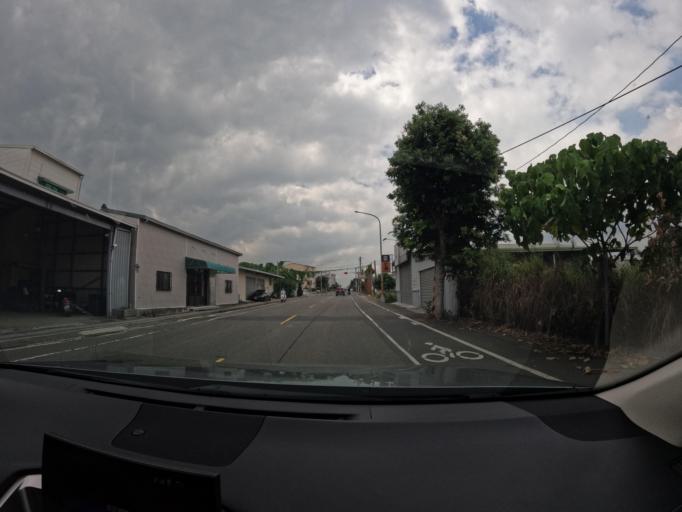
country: TW
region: Taiwan
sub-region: Nantou
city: Nantou
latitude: 23.9128
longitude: 120.6374
